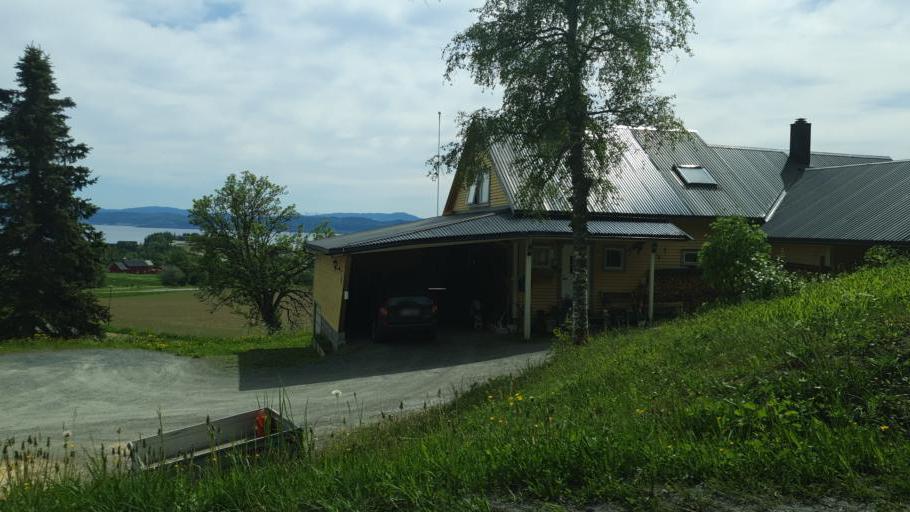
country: NO
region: Nord-Trondelag
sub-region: Leksvik
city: Leksvik
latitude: 63.6845
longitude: 10.5975
